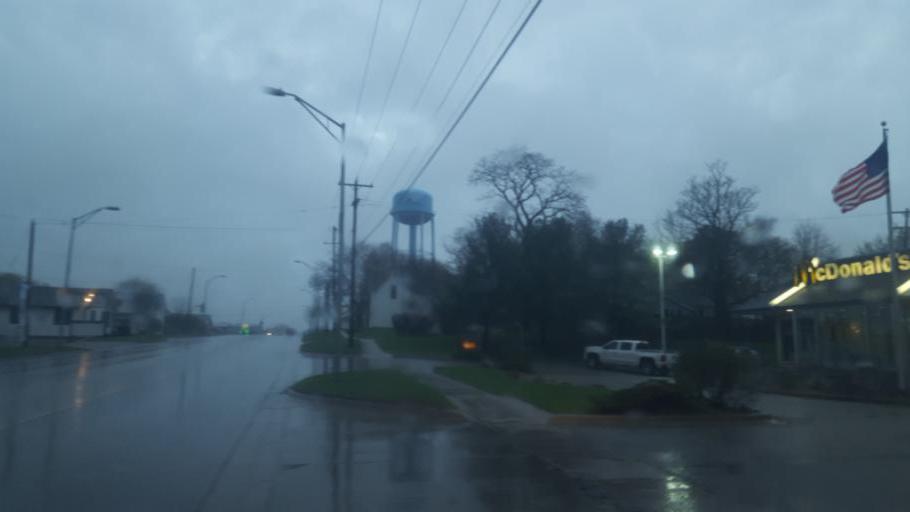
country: US
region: Michigan
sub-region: Montcalm County
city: Edmore
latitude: 43.4081
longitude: -85.0345
